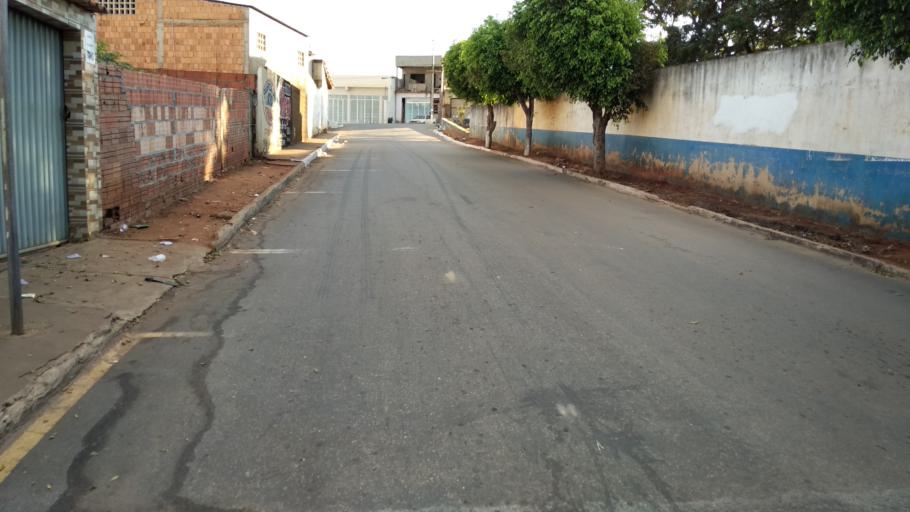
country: BR
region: Bahia
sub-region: Caetite
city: Caetite
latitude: -14.0586
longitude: -42.4831
